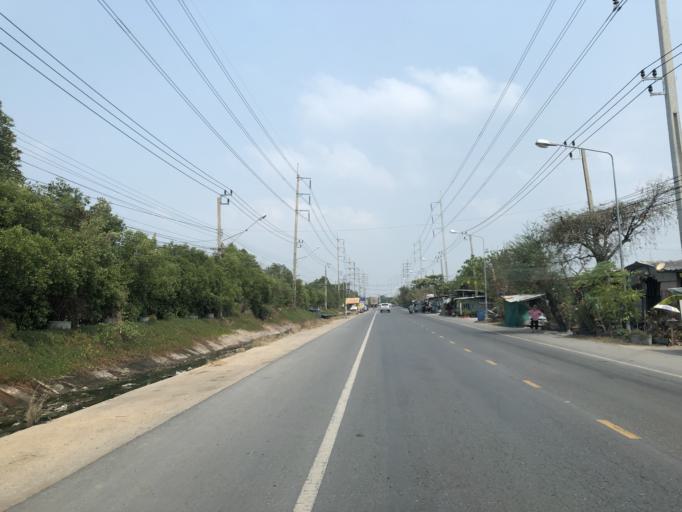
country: TH
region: Samut Prakan
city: Bang Bo
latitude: 13.5154
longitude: 100.8330
